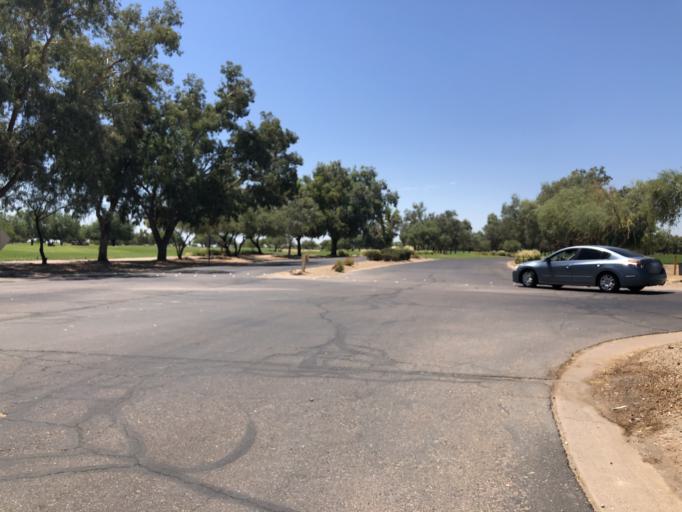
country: US
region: Arizona
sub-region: Maricopa County
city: Scottsdale
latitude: 33.5455
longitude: -111.8646
